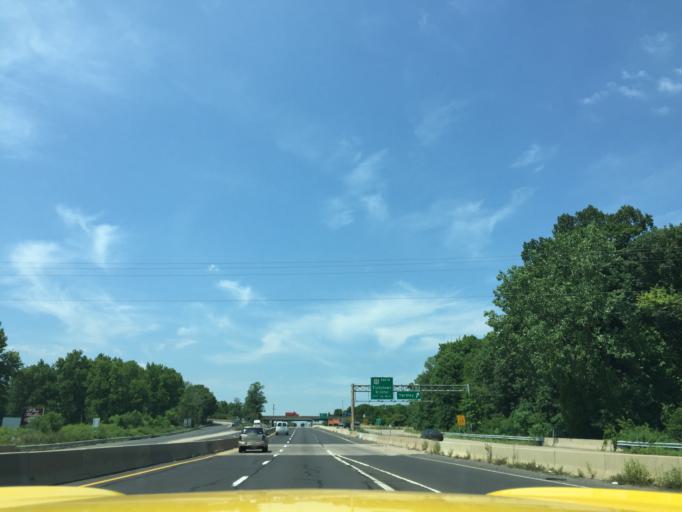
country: US
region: Pennsylvania
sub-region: Bucks County
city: Morrisville
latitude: 40.1972
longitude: -74.7973
